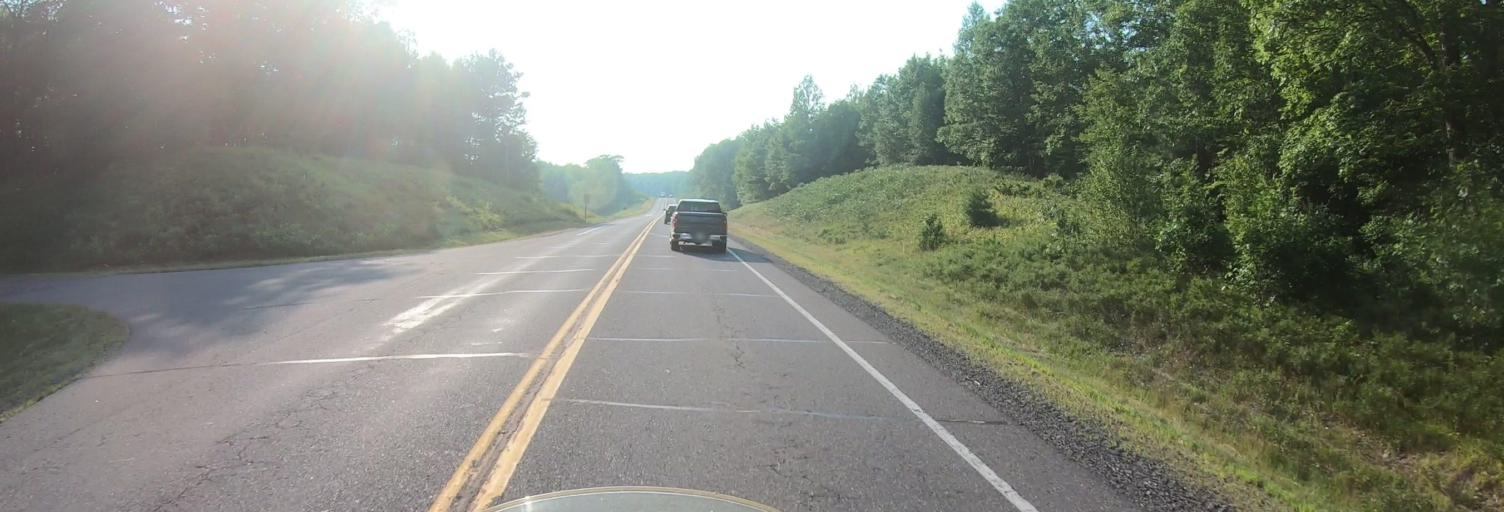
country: US
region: Wisconsin
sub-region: Sawyer County
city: Little Round Lake
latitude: 46.0657
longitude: -91.1650
